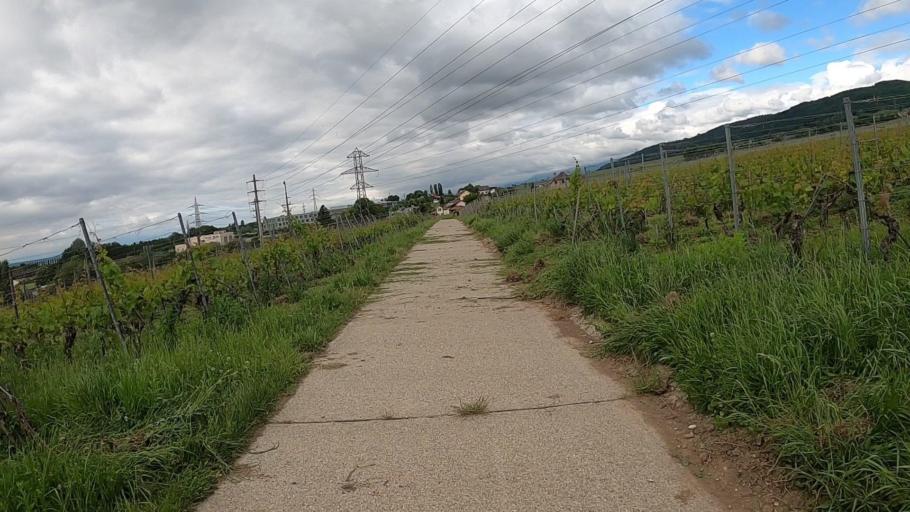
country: CH
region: Vaud
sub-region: Nyon District
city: Rolle
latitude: 46.4649
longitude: 6.3292
